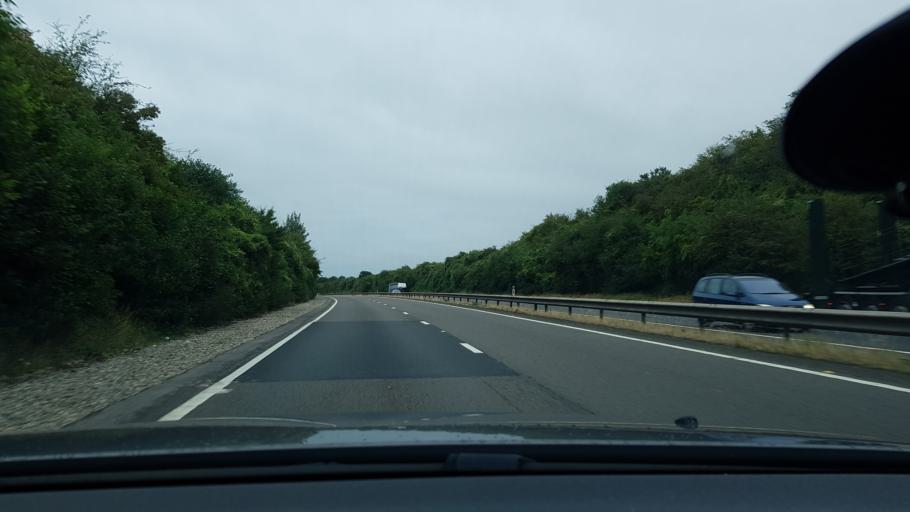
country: GB
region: England
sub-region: Hampshire
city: Overton
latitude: 51.2541
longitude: -1.3402
